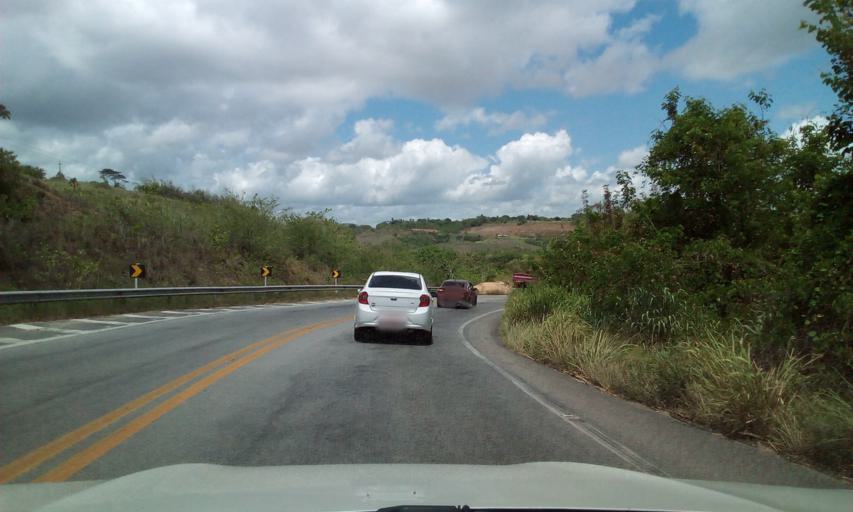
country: BR
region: Alagoas
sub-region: Pilar
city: Pilar
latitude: -9.5976
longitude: -36.0123
